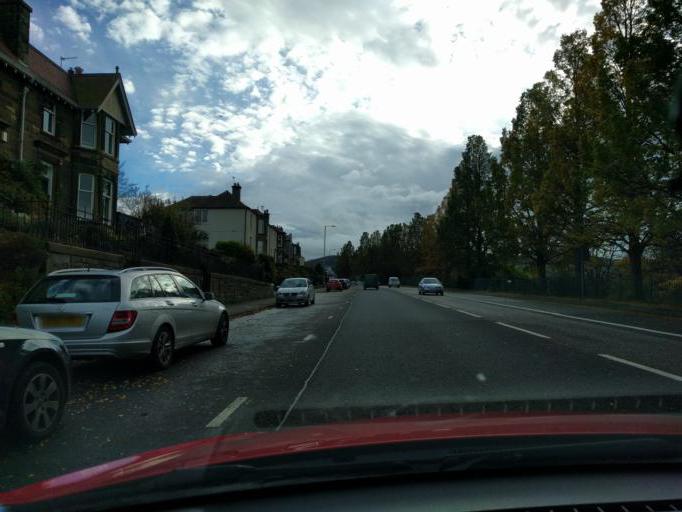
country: GB
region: Scotland
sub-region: Edinburgh
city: Edinburgh
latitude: 55.9146
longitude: -3.2136
